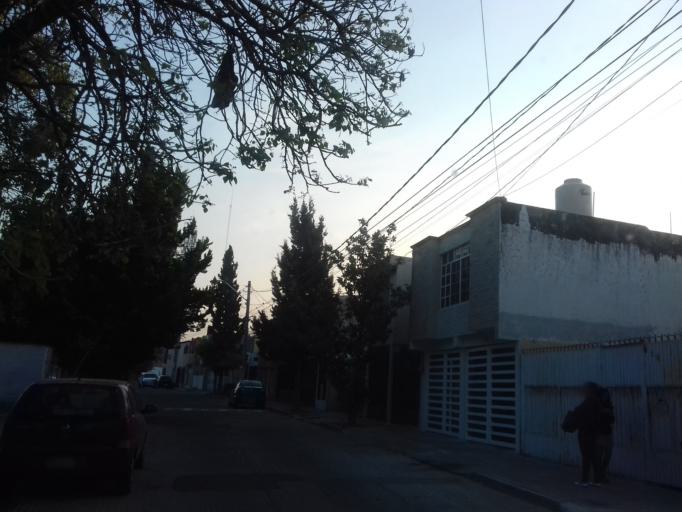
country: MX
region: Aguascalientes
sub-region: Aguascalientes
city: Aguascalientes
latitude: 21.8715
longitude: -102.2718
